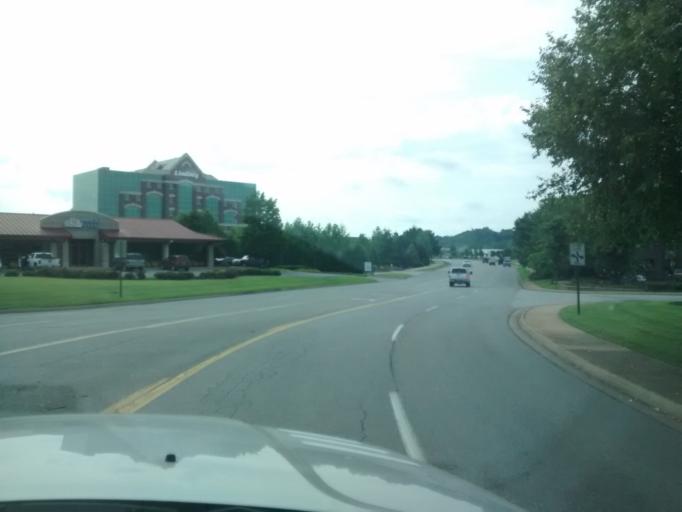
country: US
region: Arkansas
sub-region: Washington County
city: Johnson
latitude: 36.1233
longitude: -94.1429
